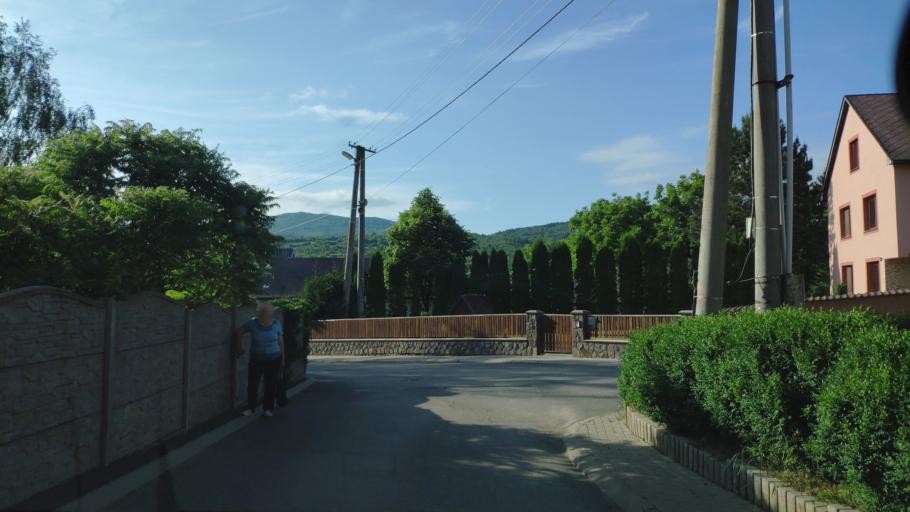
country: SK
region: Presovsky
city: Vranov nad Topl'ou
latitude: 48.8282
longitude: 21.5768
